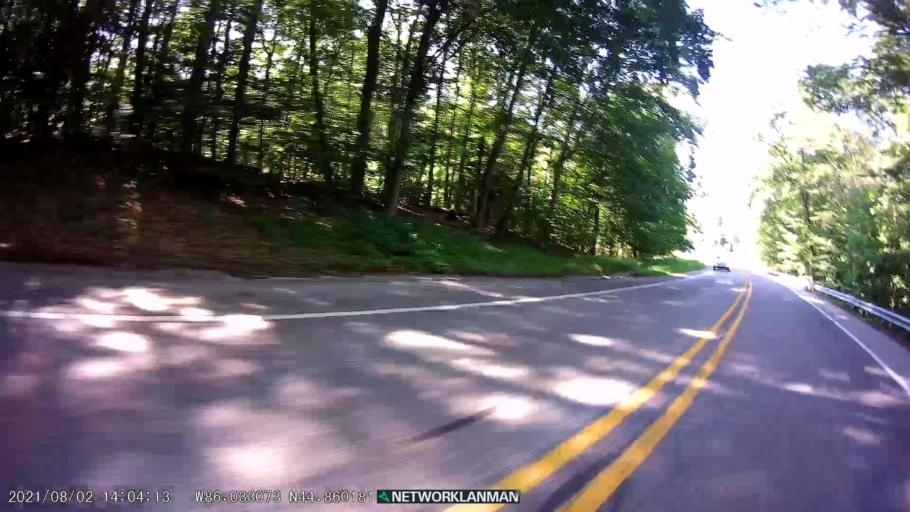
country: US
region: Michigan
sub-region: Benzie County
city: Beulah
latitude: 44.8605
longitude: -86.0331
